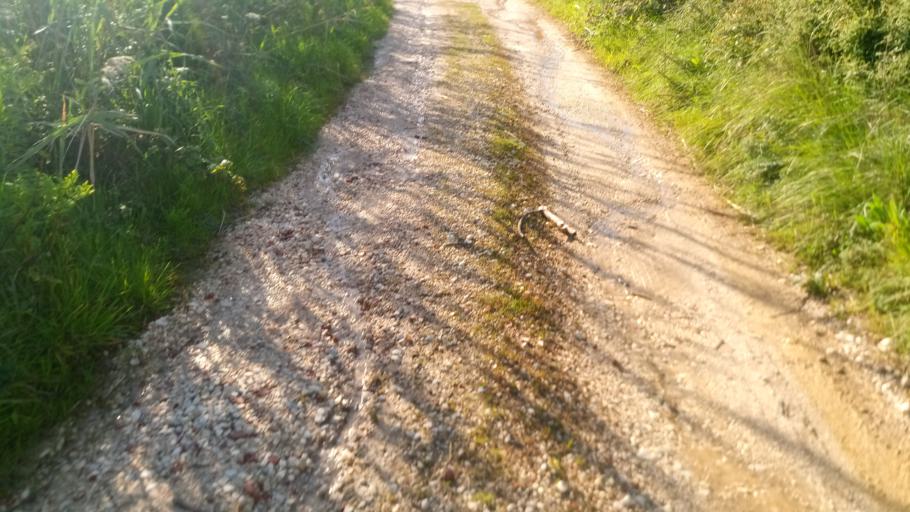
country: PT
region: Leiria
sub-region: Caldas da Rainha
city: Caldas da Rainha
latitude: 39.4627
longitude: -9.1981
